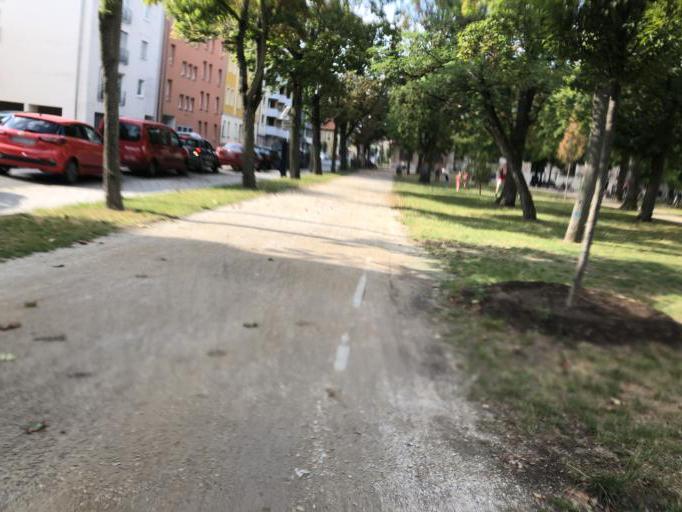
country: DE
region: Bavaria
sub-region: Regierungsbezirk Mittelfranken
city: Erlangen
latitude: 49.5931
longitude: 11.0102
